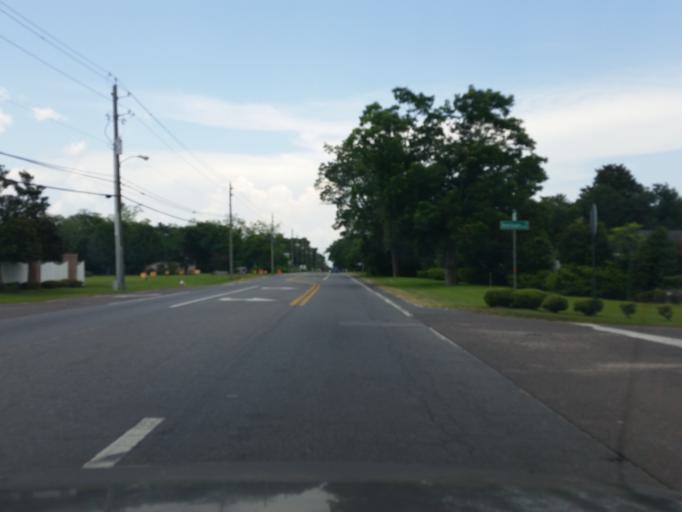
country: US
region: Florida
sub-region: Escambia County
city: Ferry Pass
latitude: 30.5108
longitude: -87.2361
